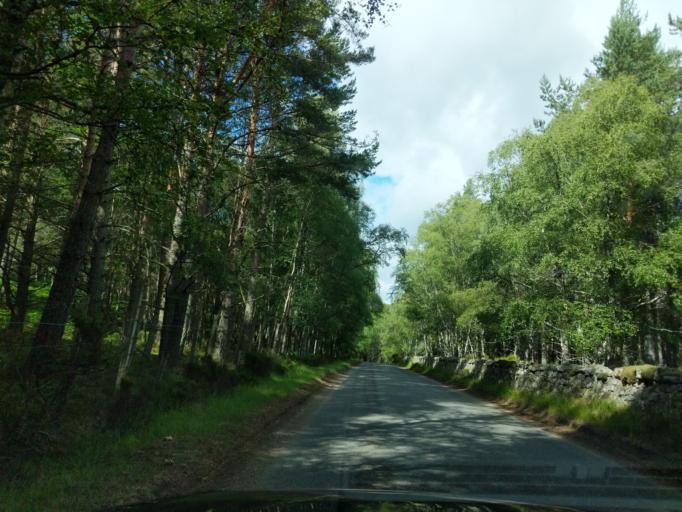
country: GB
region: Scotland
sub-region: Aberdeenshire
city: Ballater
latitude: 57.0504
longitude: -3.1399
